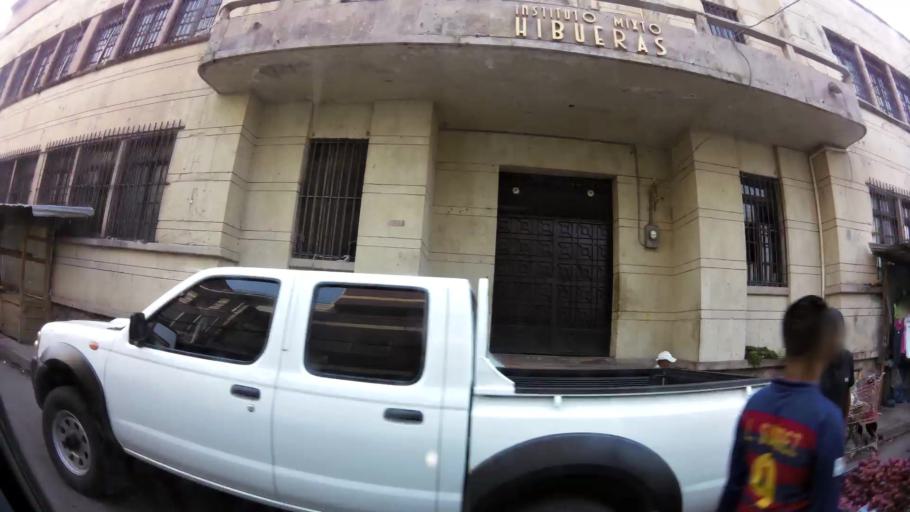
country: HN
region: Francisco Morazan
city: Tegucigalpa
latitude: 14.1018
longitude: -87.2078
